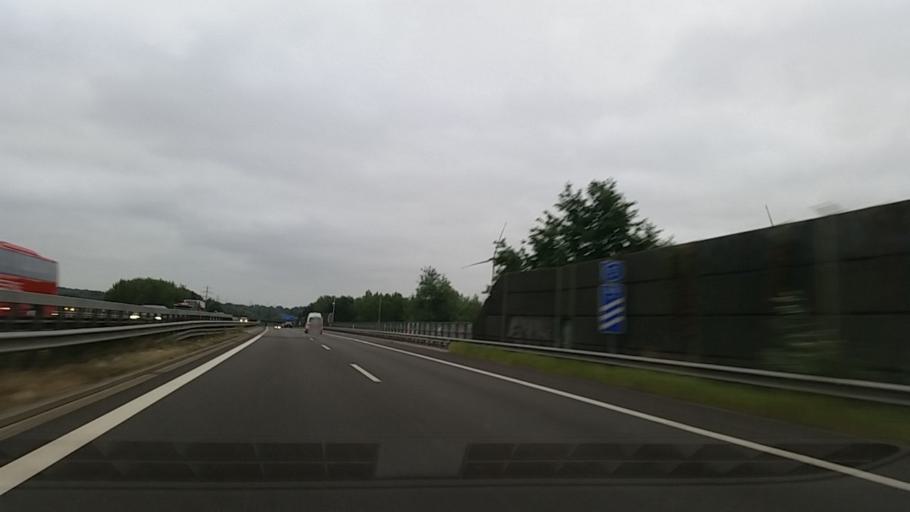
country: DE
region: Hamburg
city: Bergedorf
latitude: 53.4735
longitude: 10.1981
